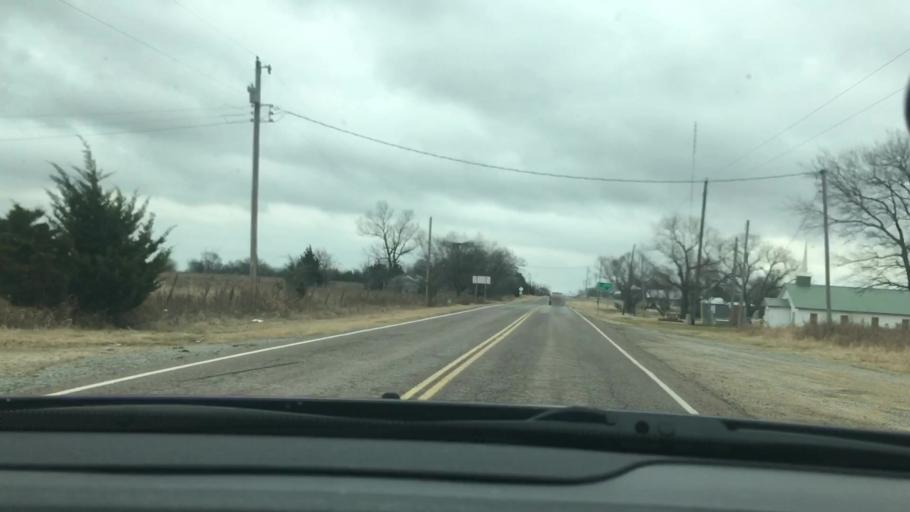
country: US
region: Oklahoma
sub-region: Bryan County
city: Durant
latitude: 34.1433
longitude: -96.5024
